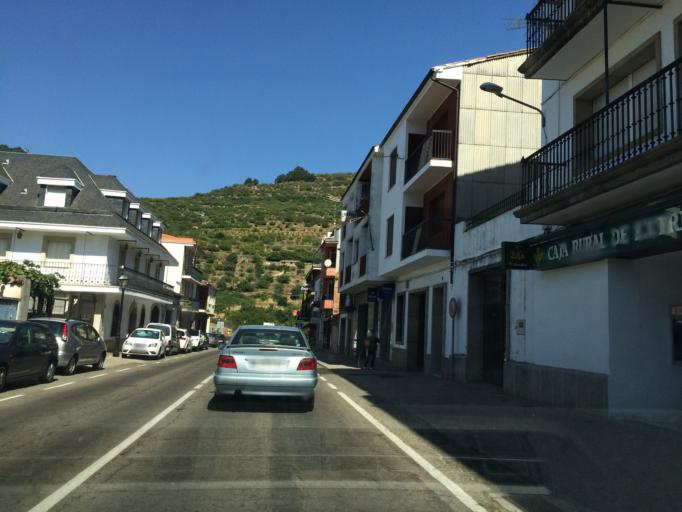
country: ES
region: Extremadura
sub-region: Provincia de Caceres
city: Cabezuela del Valle
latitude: 40.1929
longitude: -5.8075
